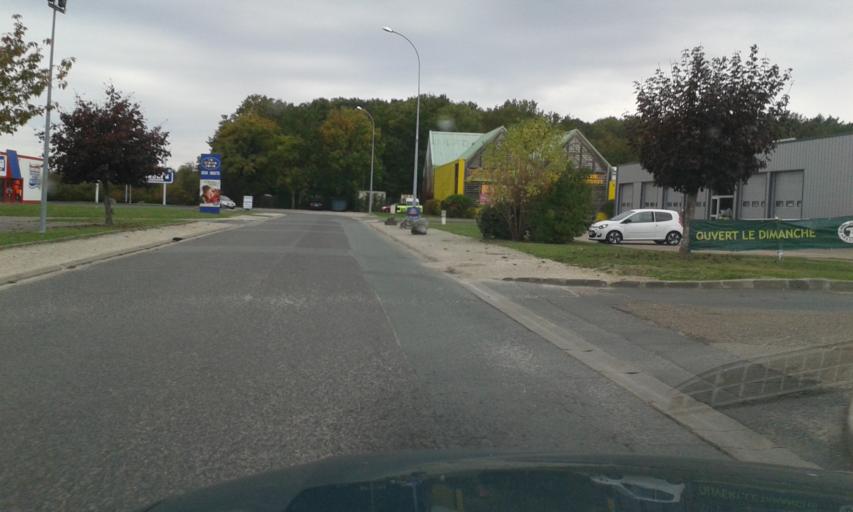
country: FR
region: Centre
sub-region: Departement du Loiret
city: Saran
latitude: 47.9638
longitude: 1.8854
